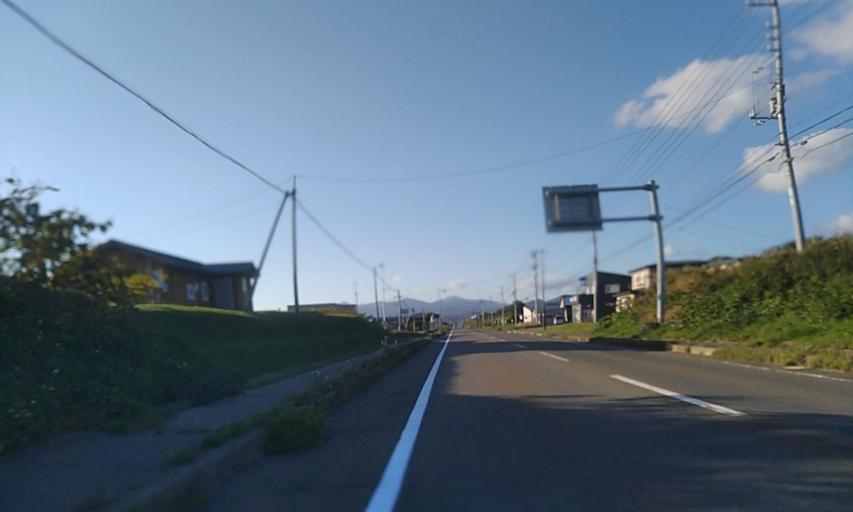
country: JP
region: Hokkaido
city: Shizunai-furukawacho
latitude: 42.0025
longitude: 143.1590
